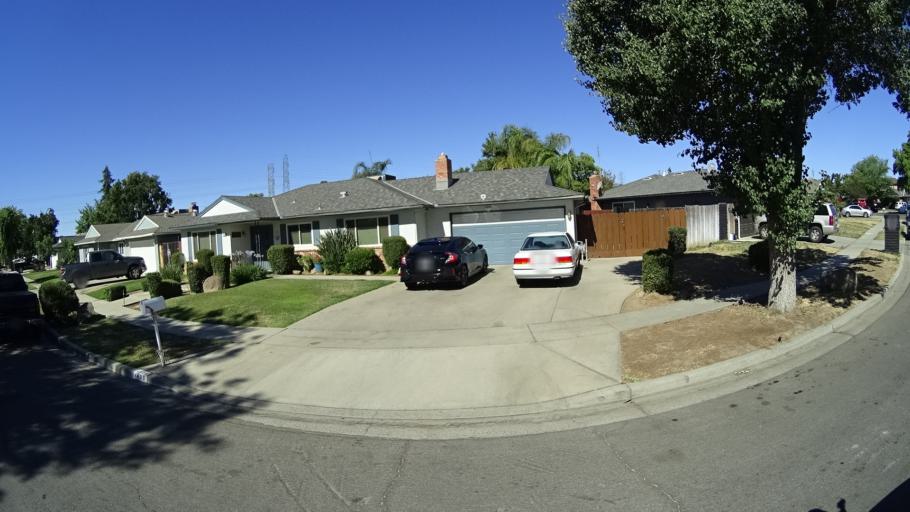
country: US
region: California
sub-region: Fresno County
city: Fresno
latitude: 36.7983
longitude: -119.8313
